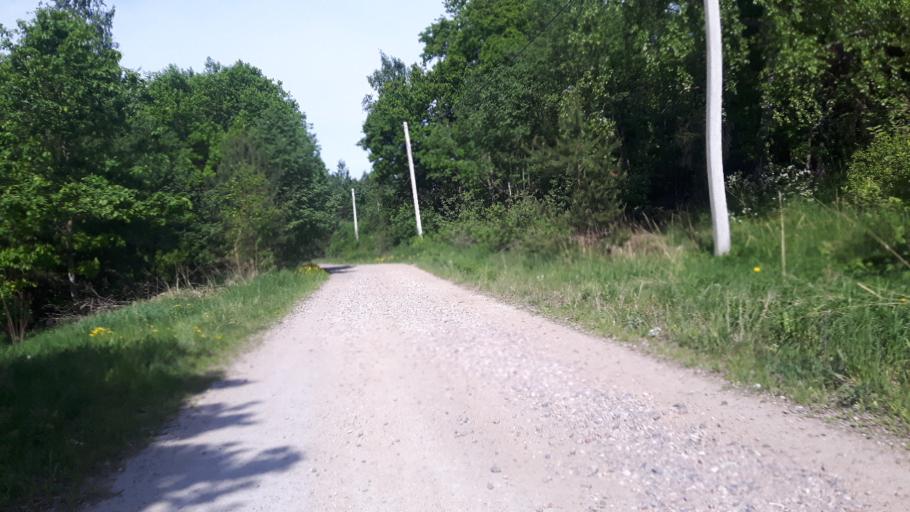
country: RU
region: Leningrad
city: Vistino
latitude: 59.6722
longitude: 28.4479
